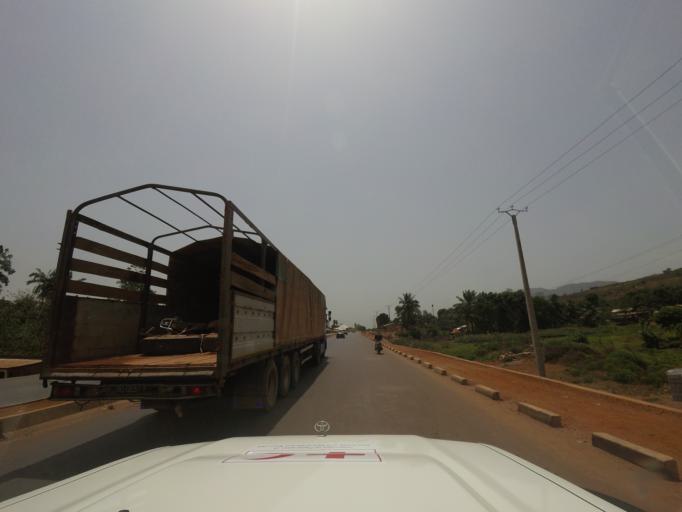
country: GN
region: Kindia
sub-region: Coyah
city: Coyah
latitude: 9.7115
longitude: -13.4014
